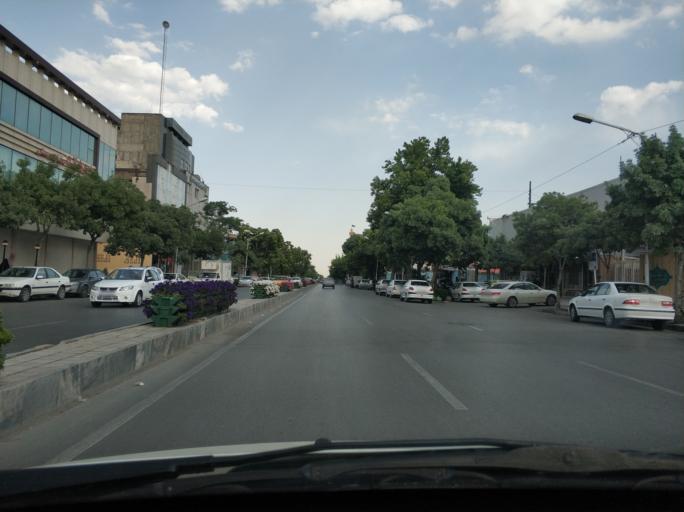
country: IR
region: Razavi Khorasan
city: Mashhad
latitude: 36.2809
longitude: 59.5962
